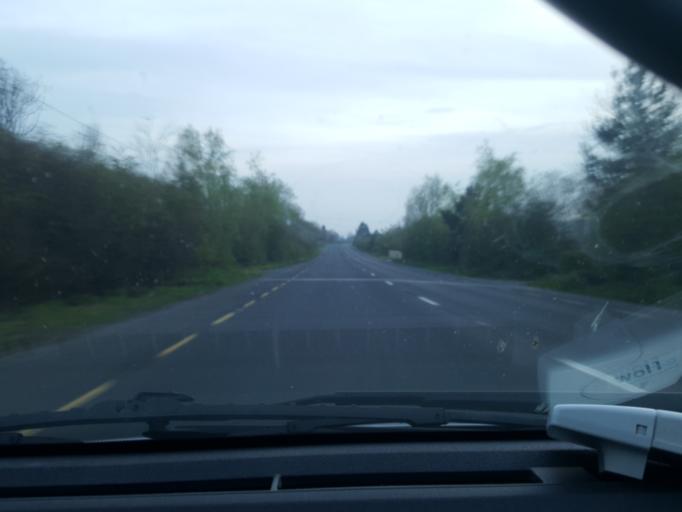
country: IE
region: Munster
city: Cahir
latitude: 52.3606
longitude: -7.9827
